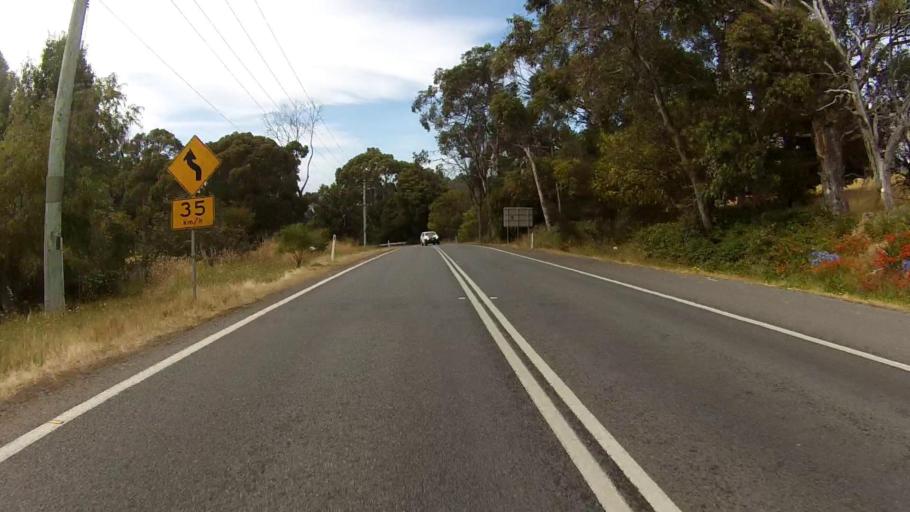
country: AU
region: Tasmania
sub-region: Kingborough
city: Kettering
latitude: -43.1305
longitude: 147.2491
